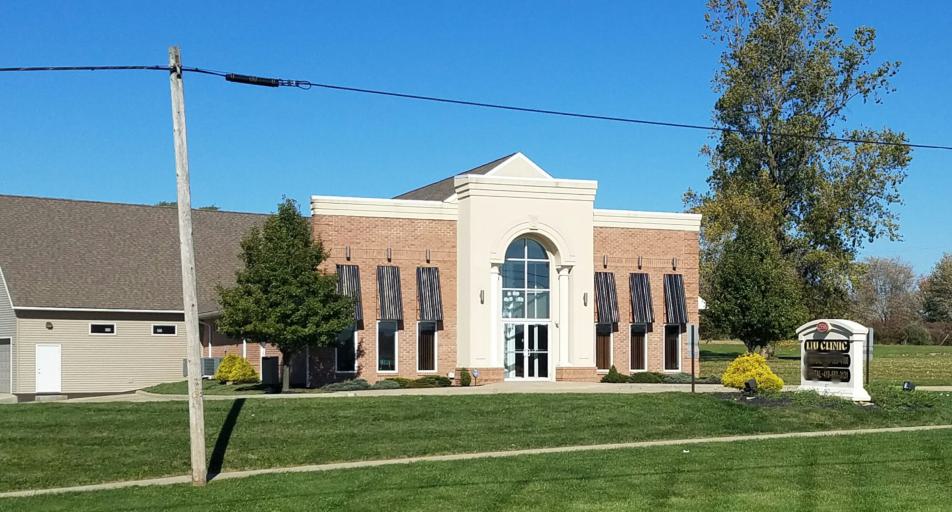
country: US
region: Ohio
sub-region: Richland County
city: Ontario
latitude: 40.7755
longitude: -82.6077
